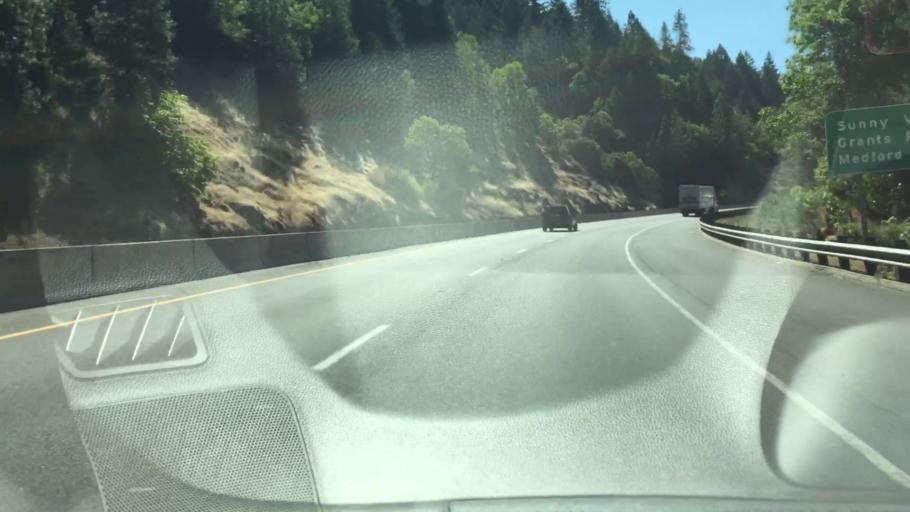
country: US
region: Oregon
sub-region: Josephine County
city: Merlin
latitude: 42.6815
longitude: -123.3850
